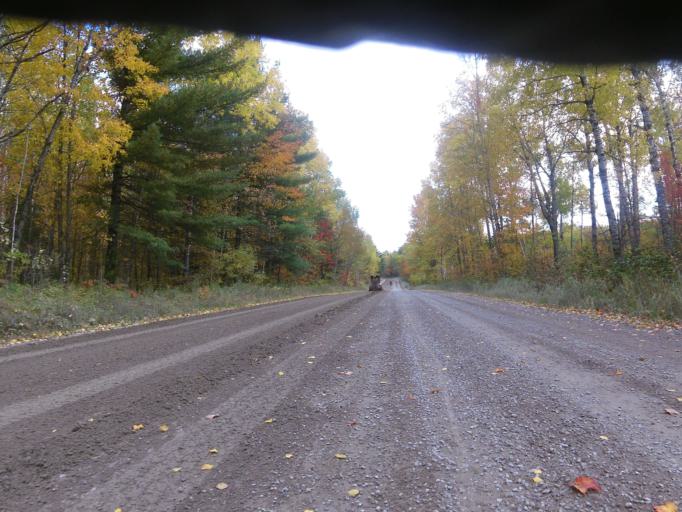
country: CA
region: Ontario
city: Petawawa
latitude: 45.8140
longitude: -77.3834
